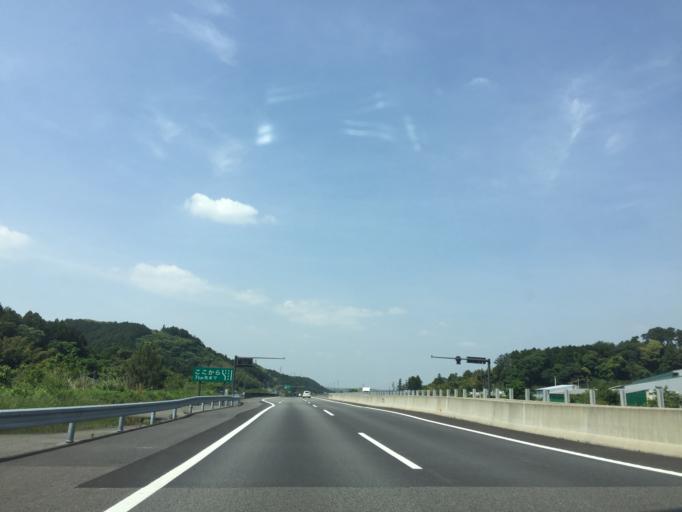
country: JP
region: Shizuoka
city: Mori
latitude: 34.8282
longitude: 137.9519
